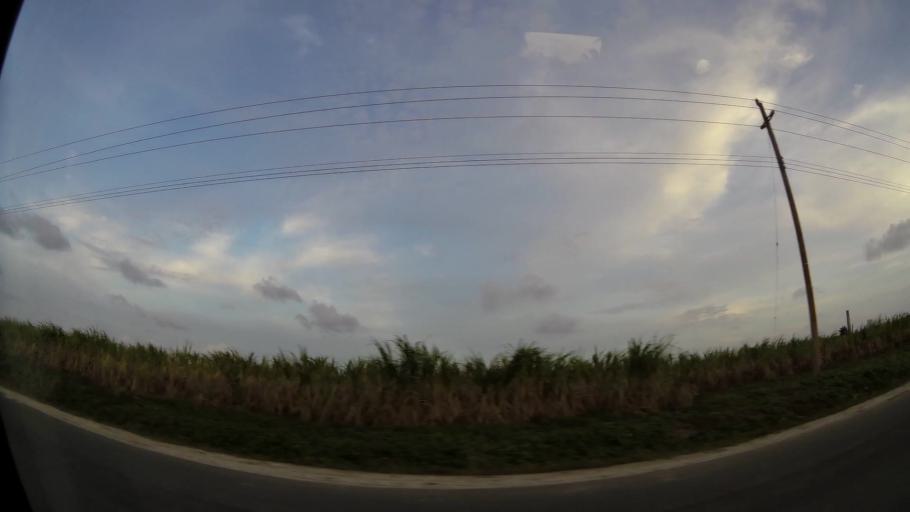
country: BB
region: Saint Philip
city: Crane
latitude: 13.1085
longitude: -59.4848
